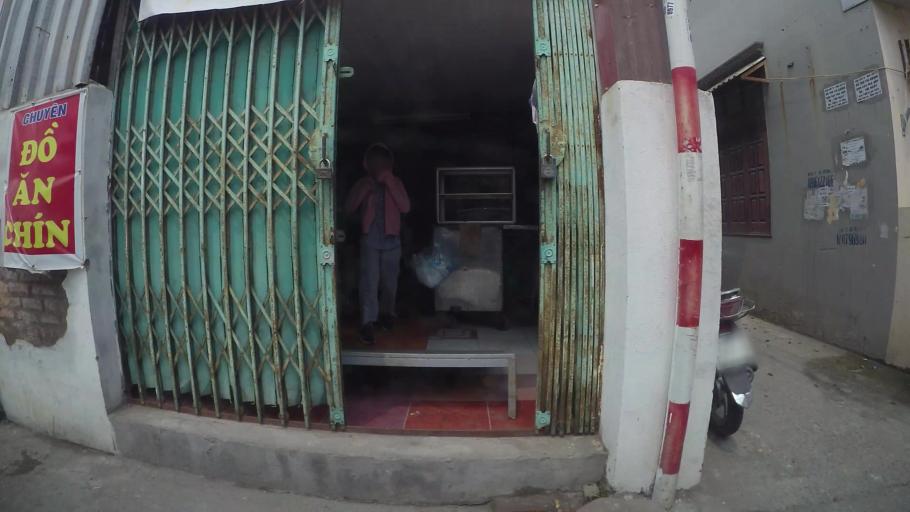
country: VN
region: Ha Noi
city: Trau Quy
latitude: 21.0695
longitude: 105.9068
